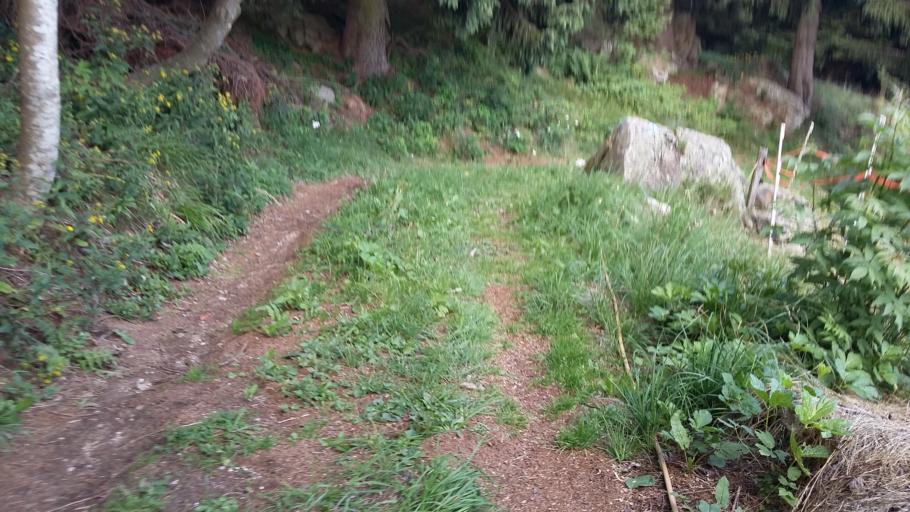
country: IT
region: Trentino-Alto Adige
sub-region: Provincia di Trento
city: Lodrone-Darzo
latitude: 45.8688
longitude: 10.5440
